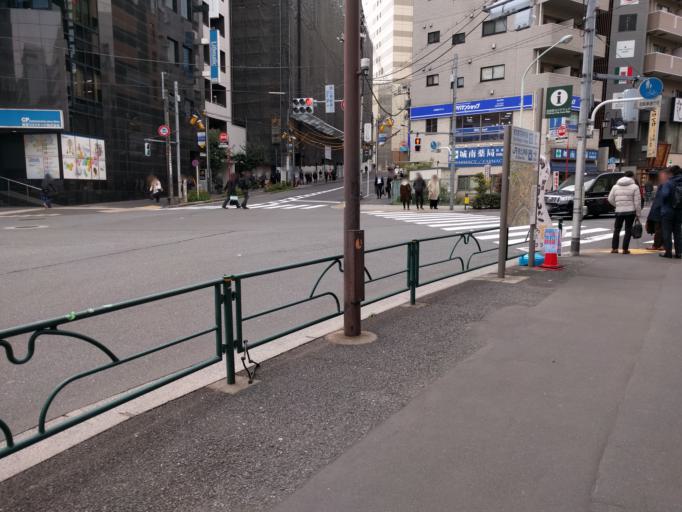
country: JP
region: Tokyo
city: Tokyo
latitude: 35.6461
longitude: 139.7125
